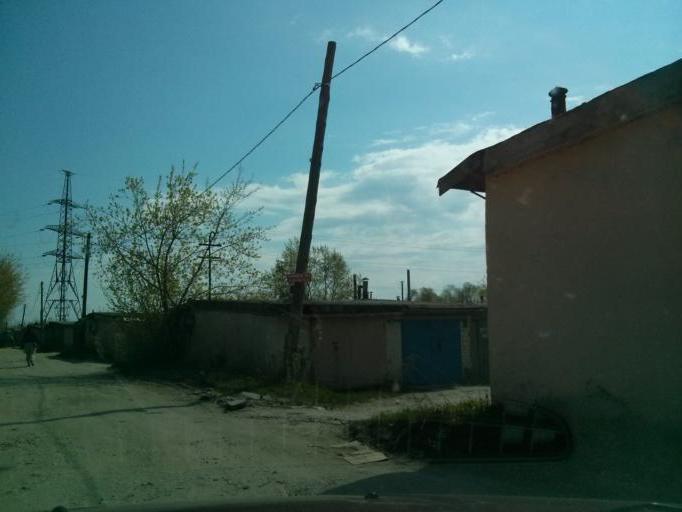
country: RU
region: Vladimir
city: Murom
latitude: 55.5638
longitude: 42.0681
